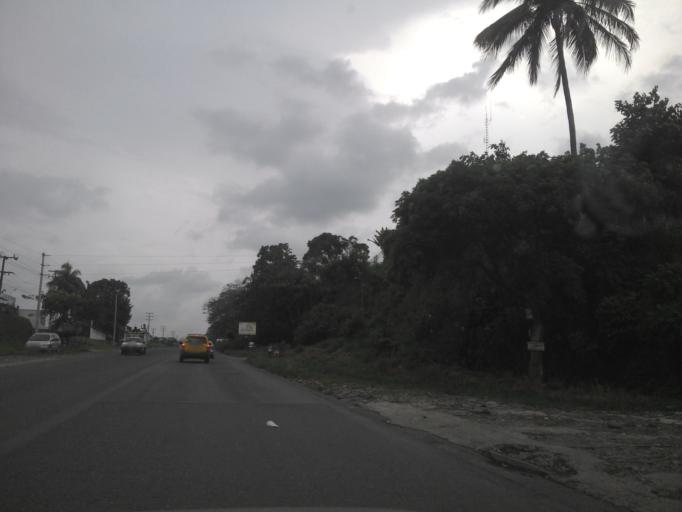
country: MX
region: Veracruz
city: Martinez de la Torre
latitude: 20.0802
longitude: -97.0381
